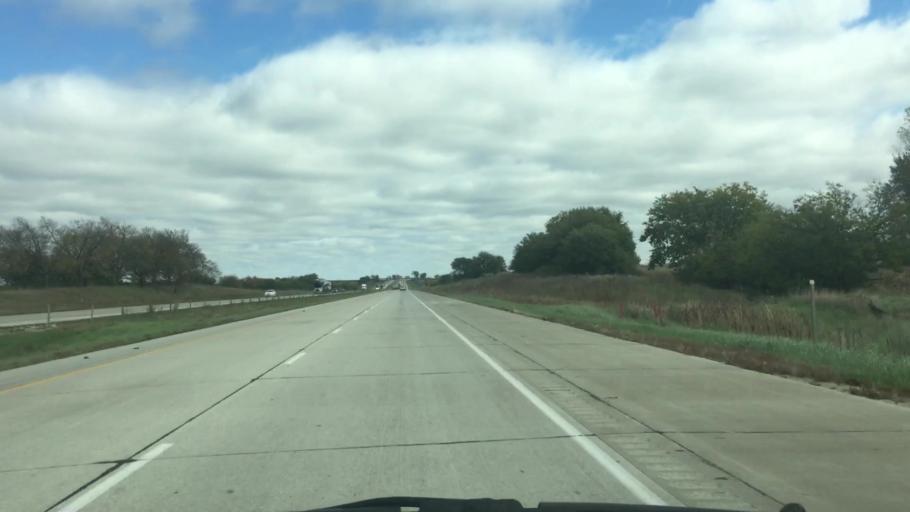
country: US
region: Iowa
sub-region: Polk County
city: Bondurant
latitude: 41.6751
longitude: -93.4263
